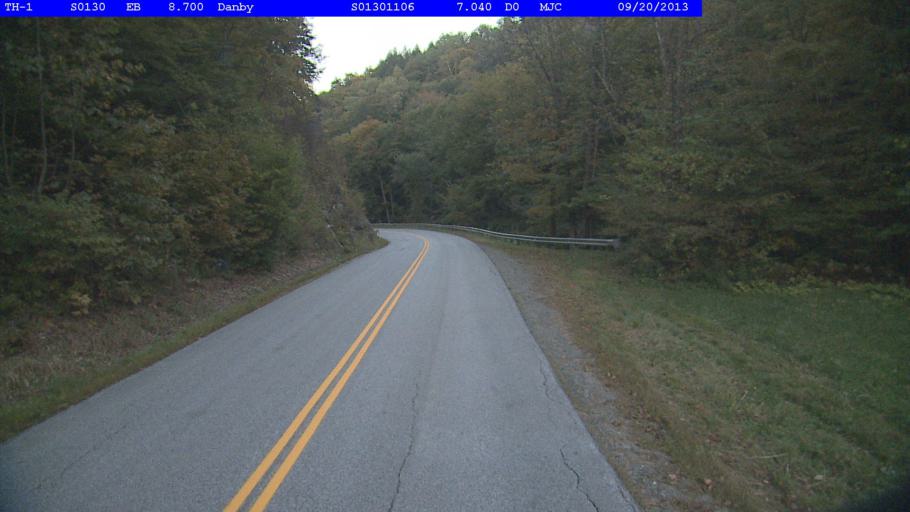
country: US
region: Vermont
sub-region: Bennington County
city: Manchester Center
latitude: 43.3370
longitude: -73.0171
